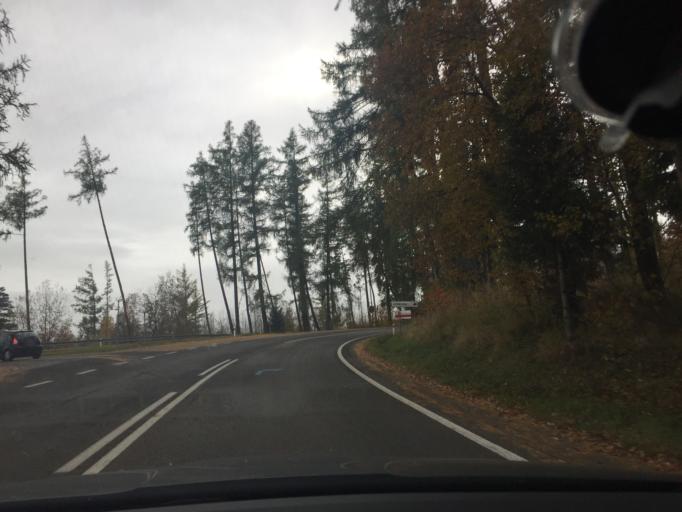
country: SK
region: Presovsky
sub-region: Okres Poprad
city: Strba
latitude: 49.1177
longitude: 20.1265
